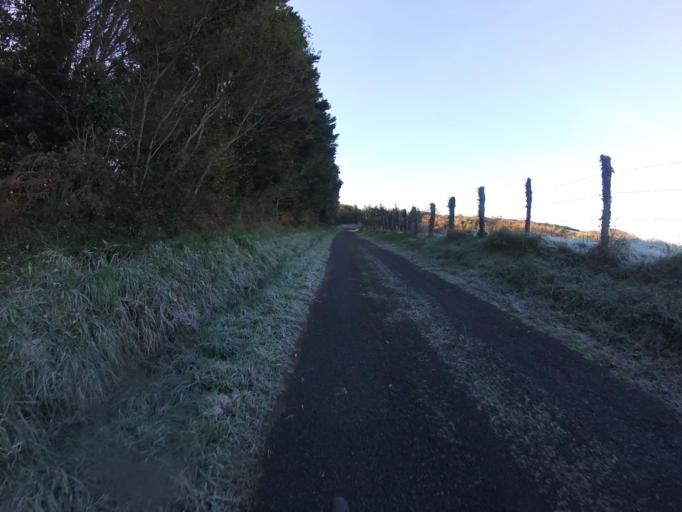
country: FR
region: Aquitaine
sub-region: Departement des Pyrenees-Atlantiques
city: Urrugne
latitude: 43.3792
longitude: -1.7062
